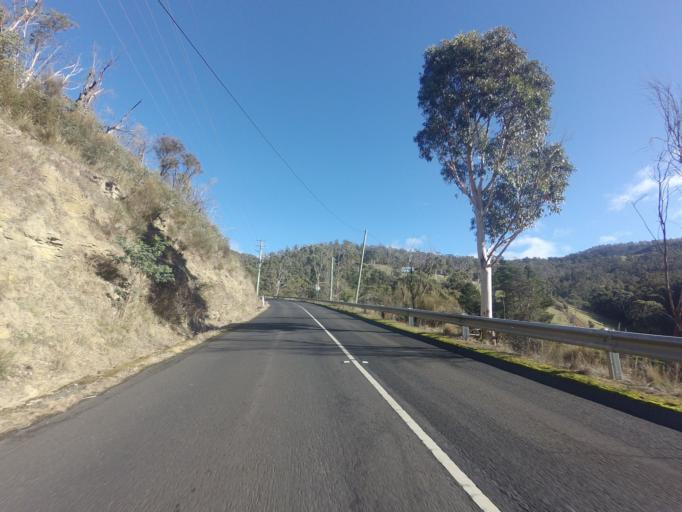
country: AU
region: Tasmania
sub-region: Glenorchy
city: Berriedale
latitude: -42.8206
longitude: 147.2129
